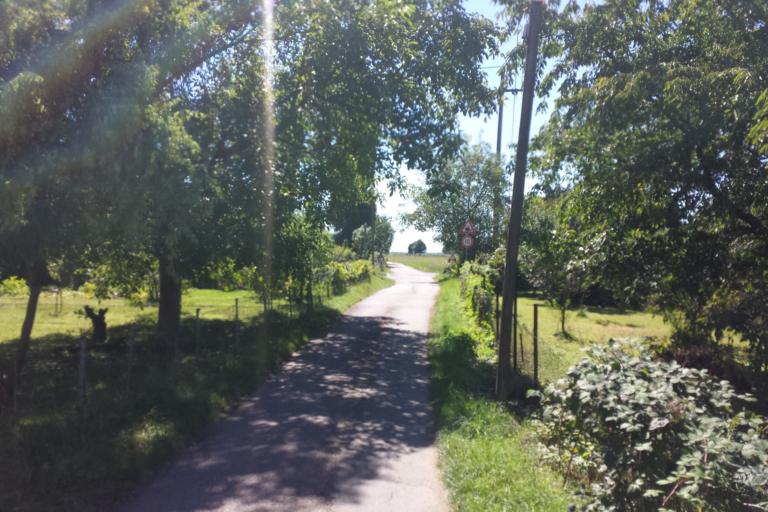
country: DE
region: Baden-Wuerttemberg
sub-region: Karlsruhe Region
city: Edingen-Neckarhausen
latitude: 49.4383
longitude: 8.6249
